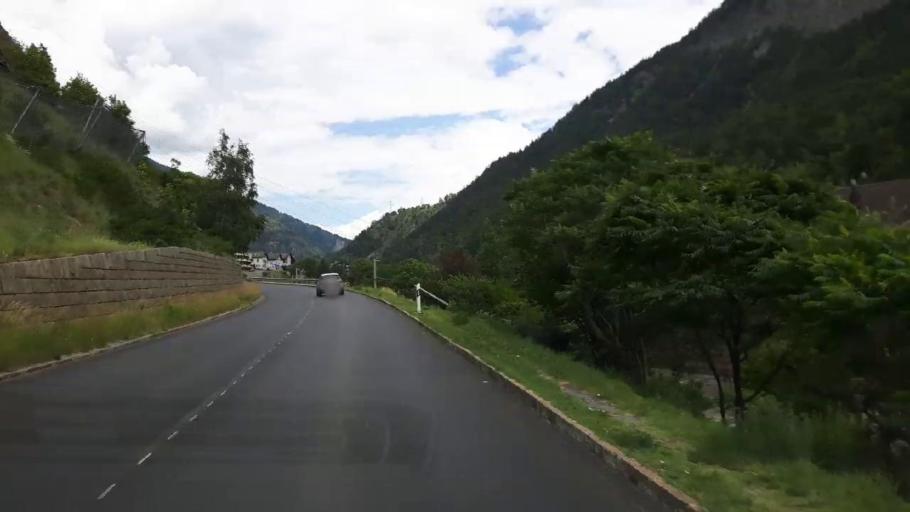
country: CH
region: Valais
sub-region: Brig District
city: Naters
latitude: 46.3518
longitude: 8.0389
